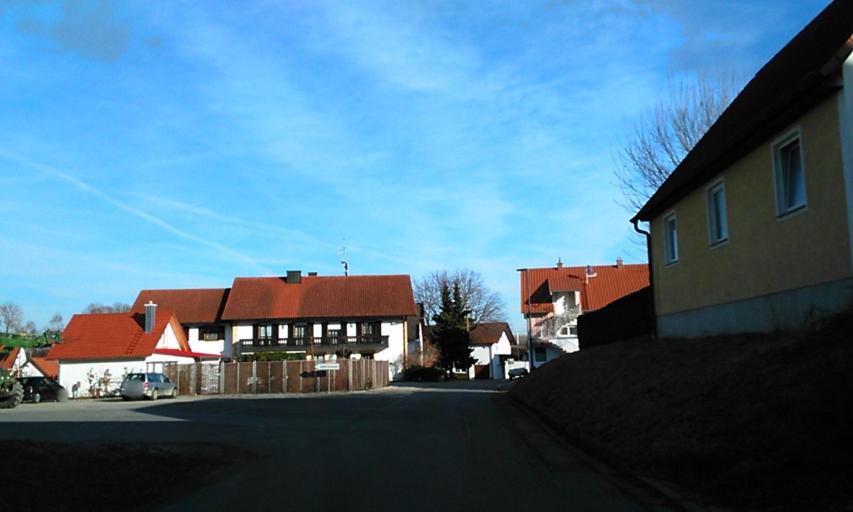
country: DE
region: Bavaria
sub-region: Swabia
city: Steindorf
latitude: 48.2172
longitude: 11.0022
